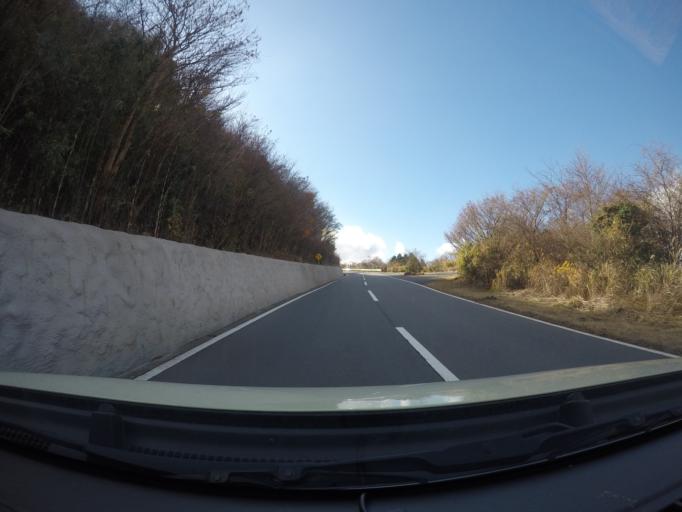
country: JP
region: Kanagawa
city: Hakone
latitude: 35.2272
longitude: 138.9804
